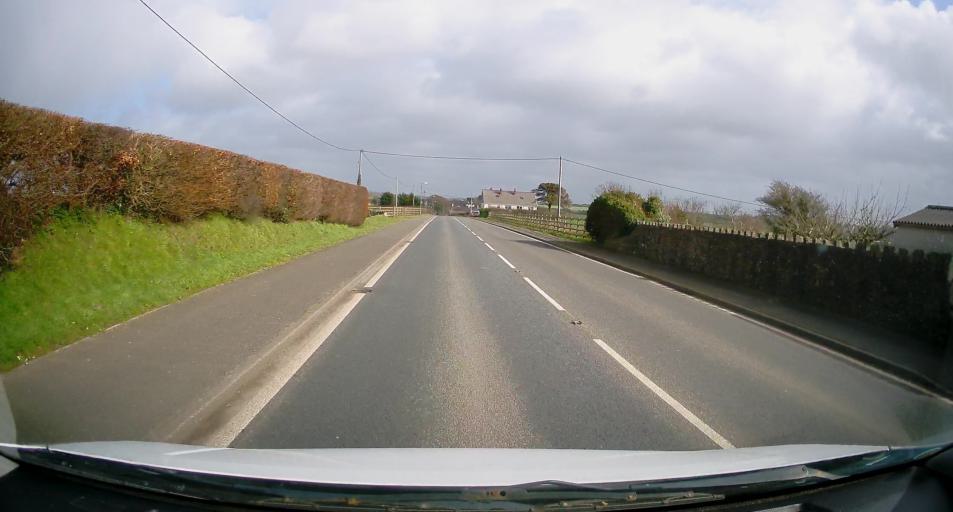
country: GB
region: Wales
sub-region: County of Ceredigion
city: Aberporth
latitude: 52.1121
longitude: -4.5599
